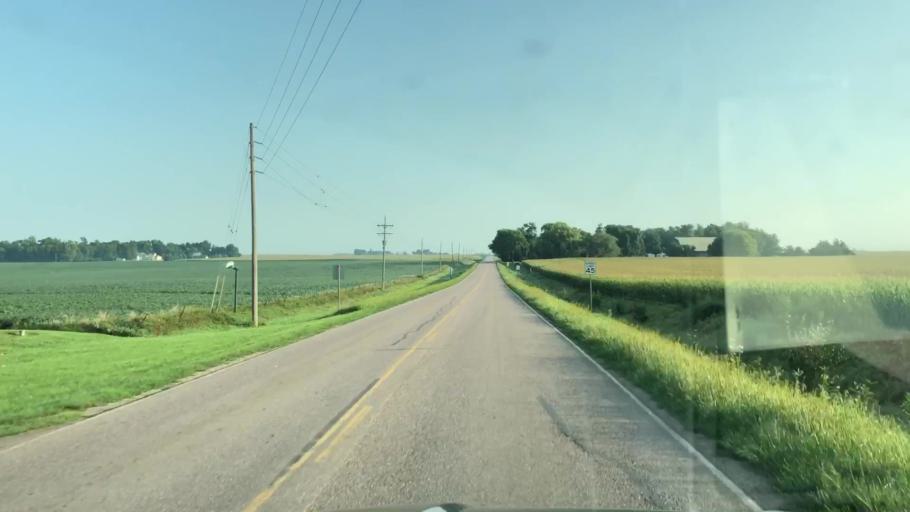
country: US
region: Iowa
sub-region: Sioux County
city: Hull
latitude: 43.1936
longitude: -96.0003
